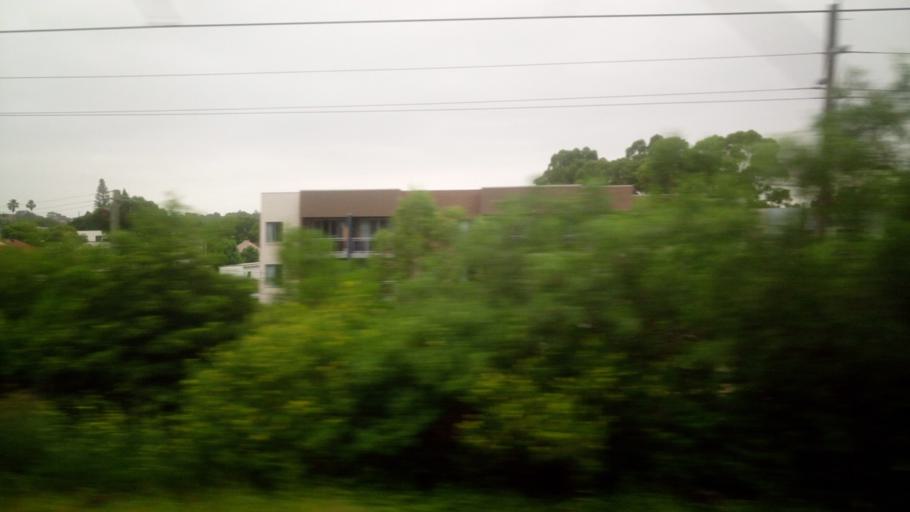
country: AU
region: New South Wales
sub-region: Parramatta
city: Constitution Hill
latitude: -33.8078
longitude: 150.9745
